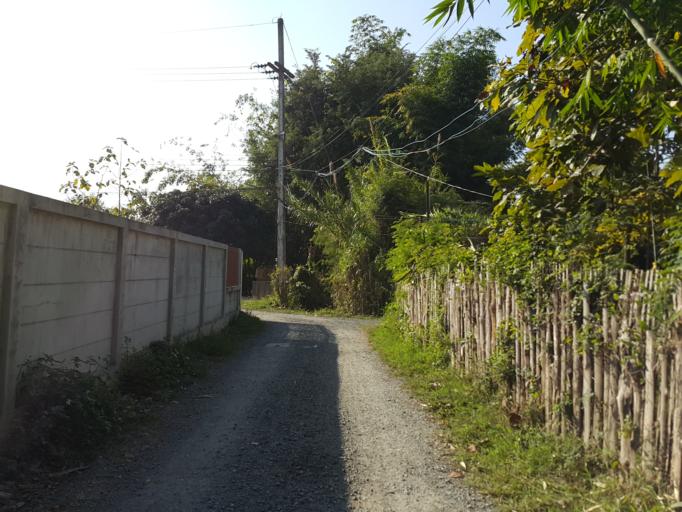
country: TH
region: Chiang Mai
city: San Kamphaeng
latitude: 18.8039
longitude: 99.1101
